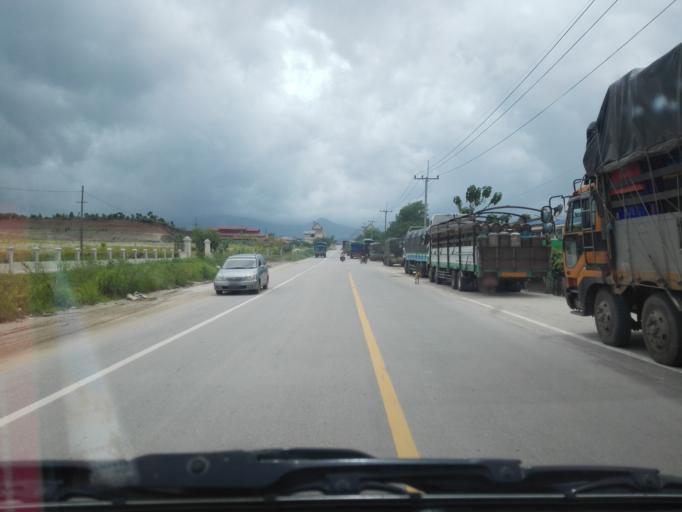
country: TH
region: Tak
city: Mae Sot
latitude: 16.6956
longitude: 98.4276
